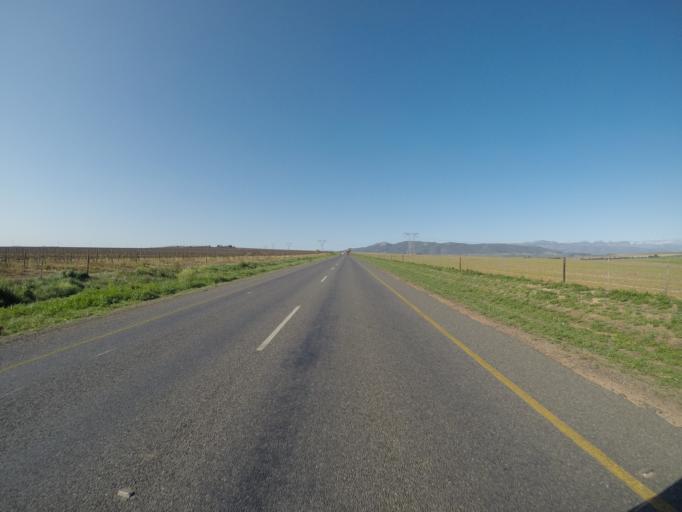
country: ZA
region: Western Cape
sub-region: City of Cape Town
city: Kraaifontein
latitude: -33.7558
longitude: 18.8162
